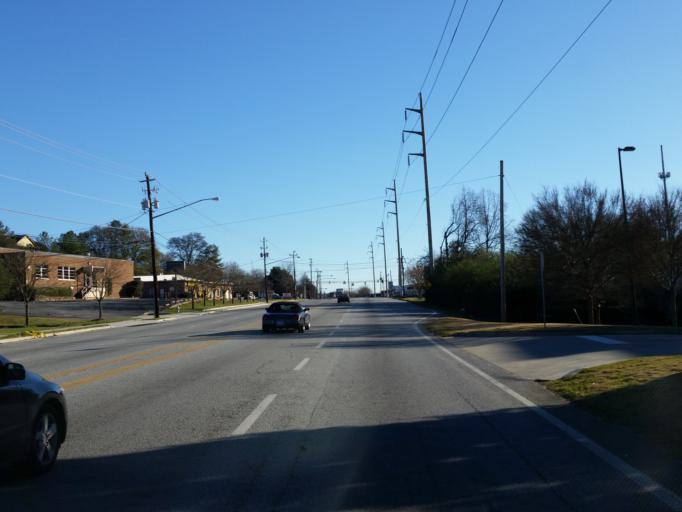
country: US
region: Georgia
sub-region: Cobb County
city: Vinings
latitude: 33.8047
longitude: -84.4372
